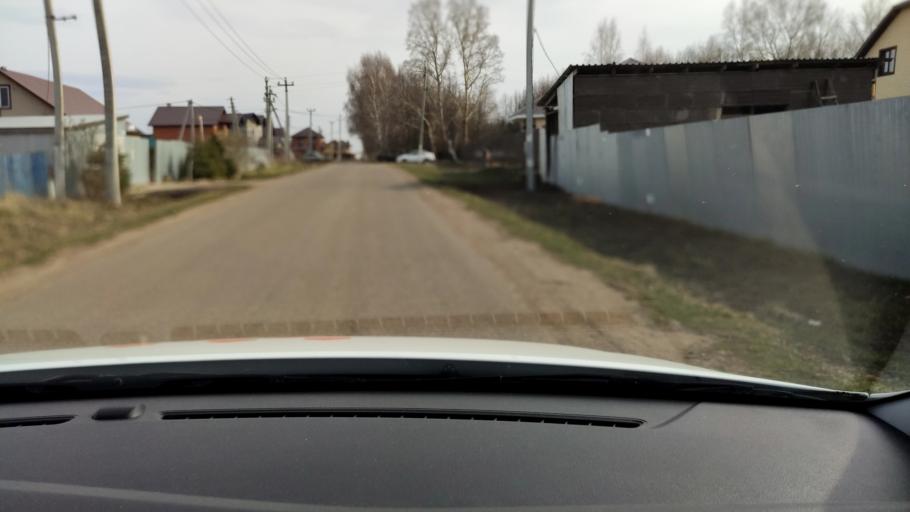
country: RU
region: Tatarstan
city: Stolbishchi
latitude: 55.6453
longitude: 49.3118
